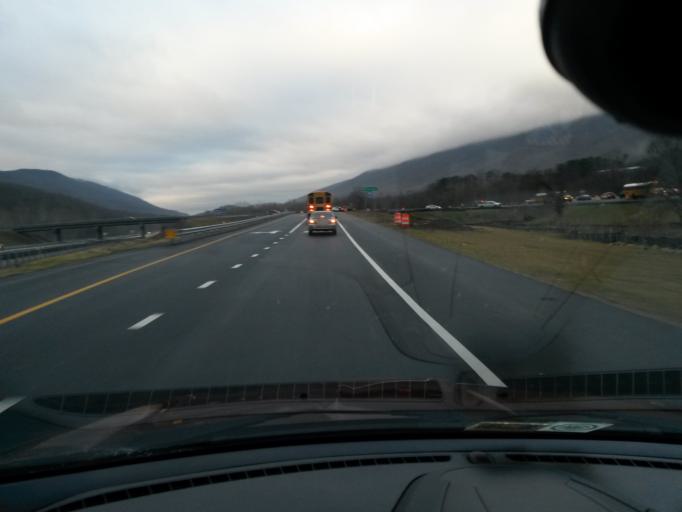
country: US
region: Virginia
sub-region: Alleghany County
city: Clifton Forge
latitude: 37.7933
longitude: -79.8836
